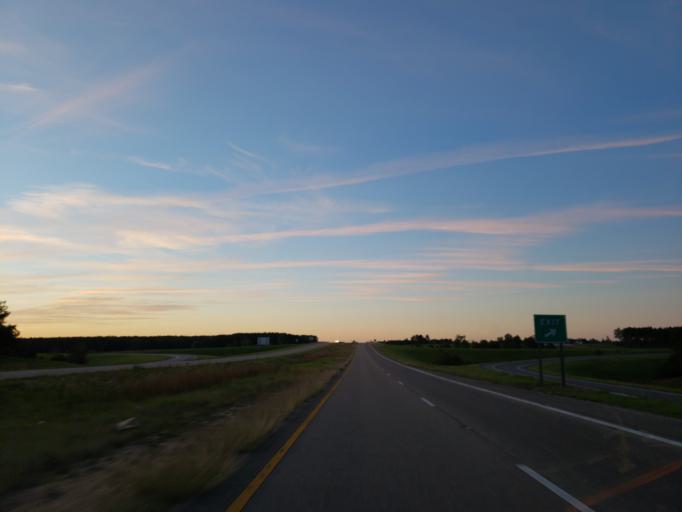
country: US
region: Mississippi
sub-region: Wayne County
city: Waynesboro
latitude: 31.7041
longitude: -88.6233
